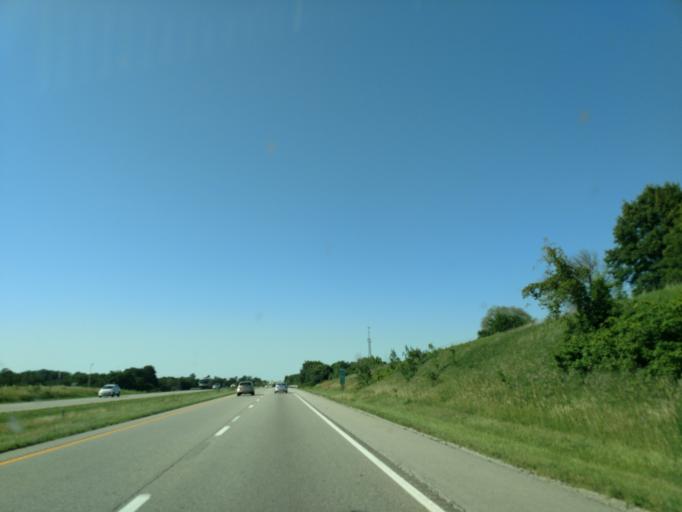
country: US
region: Missouri
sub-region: Buchanan County
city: Saint Joseph
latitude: 39.6235
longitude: -94.7881
